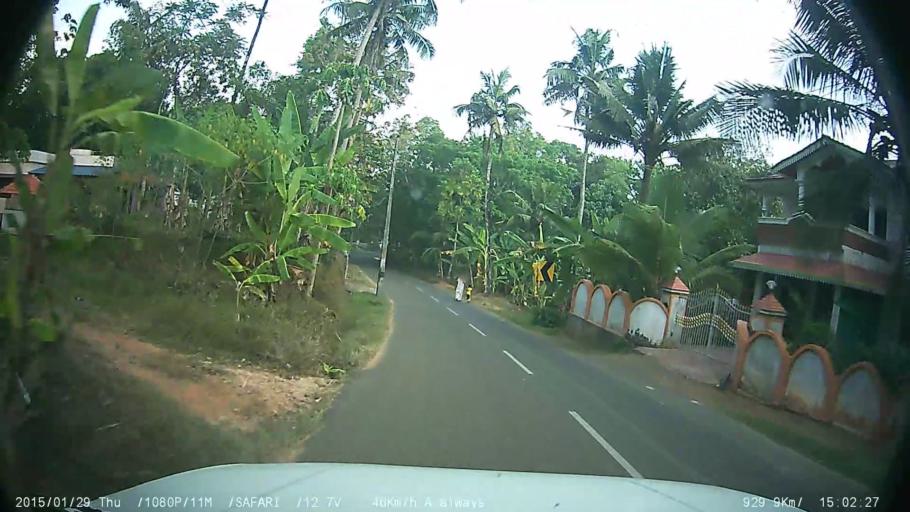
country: IN
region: Kerala
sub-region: Kottayam
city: Palackattumala
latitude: 9.7268
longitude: 76.5755
